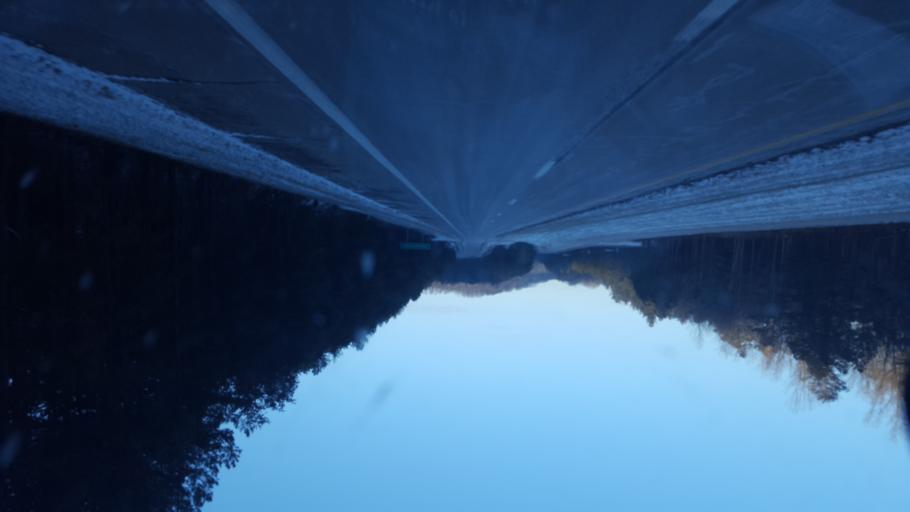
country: US
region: Ohio
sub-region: Adams County
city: Peebles
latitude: 39.0062
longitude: -83.2966
